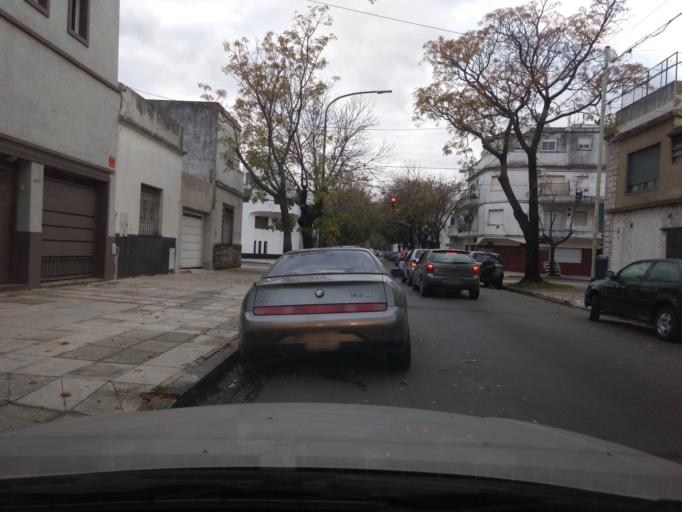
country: AR
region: Buenos Aires F.D.
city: Villa Santa Rita
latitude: -34.6094
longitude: -58.5107
